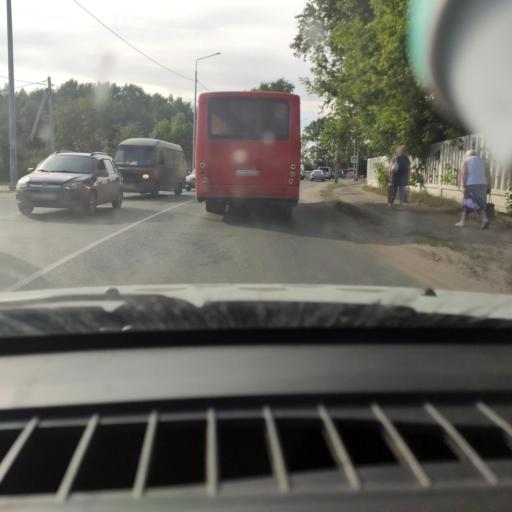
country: RU
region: Kirov
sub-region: Kirovo-Chepetskiy Rayon
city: Kirov
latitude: 58.6140
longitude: 49.7426
